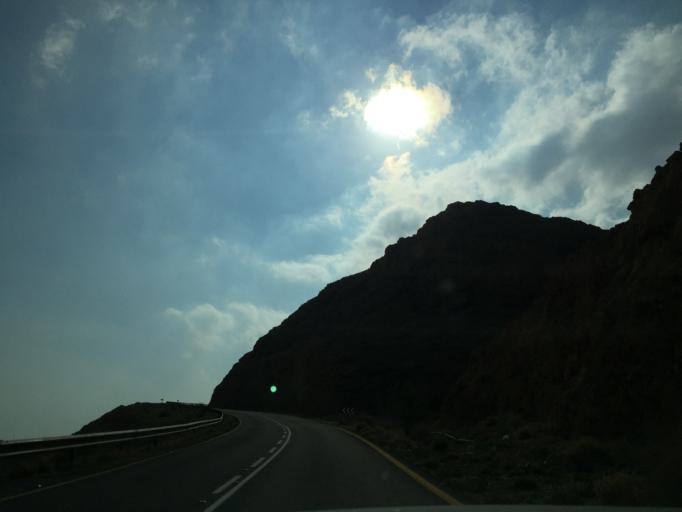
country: IL
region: Southern District
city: `En Boqeq
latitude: 31.3219
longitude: 35.3326
